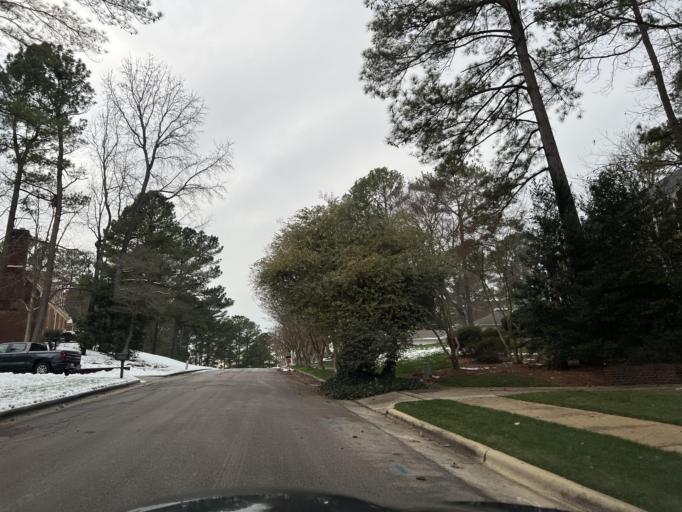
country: US
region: North Carolina
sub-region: Wake County
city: West Raleigh
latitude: 35.8731
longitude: -78.6020
